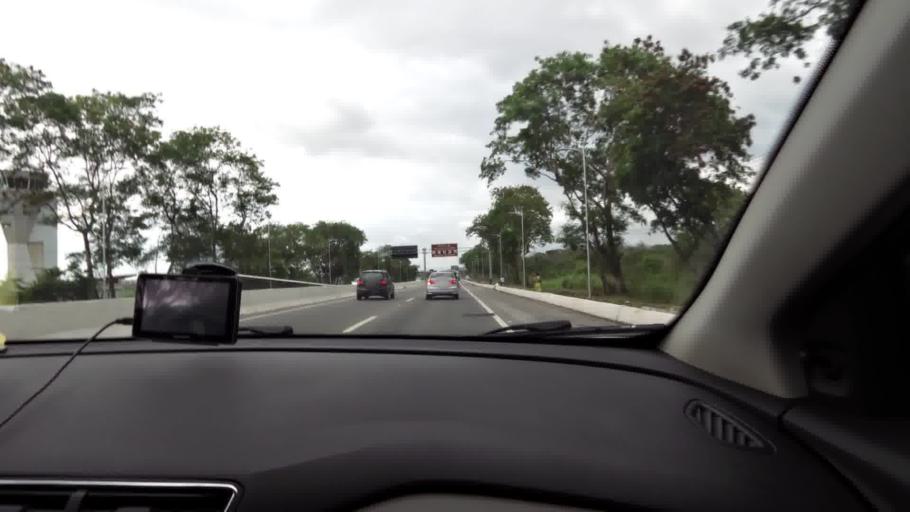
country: BR
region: Espirito Santo
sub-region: Vila Velha
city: Vila Velha
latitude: -20.2512
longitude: -40.2869
